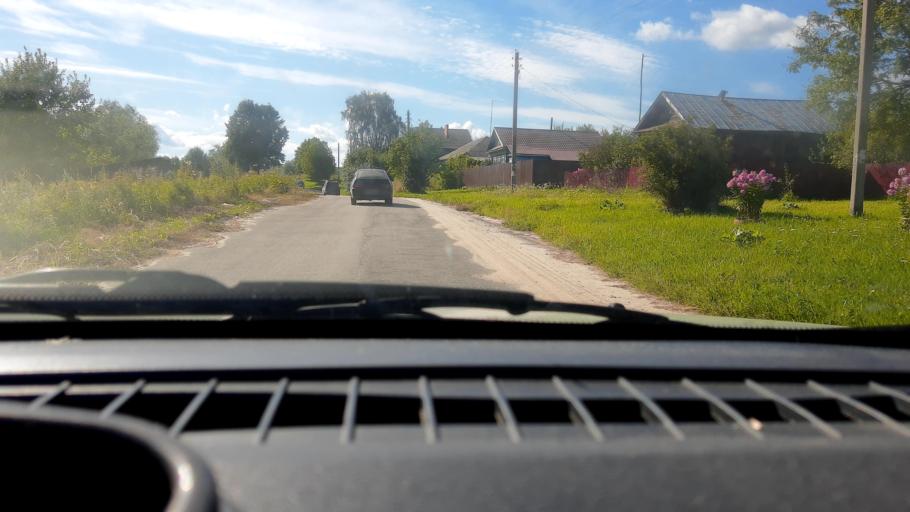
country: RU
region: Nizjnij Novgorod
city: Babino
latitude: 56.1807
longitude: 43.6021
